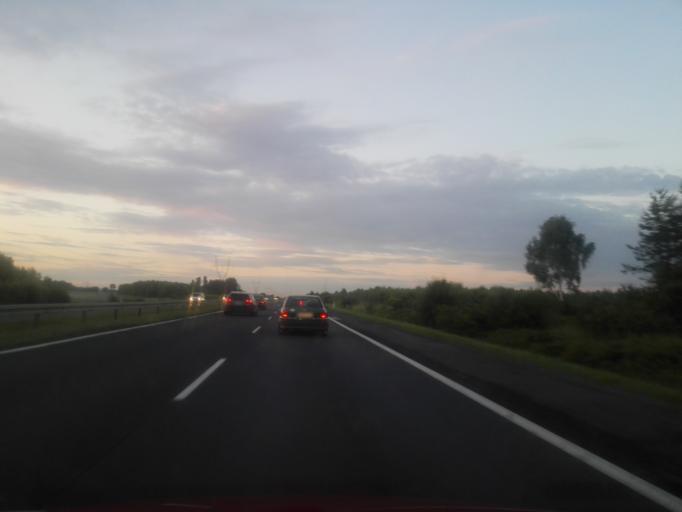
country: PL
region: Lodz Voivodeship
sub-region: Powiat radomszczanski
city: Radomsko
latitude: 51.1172
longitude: 19.4001
